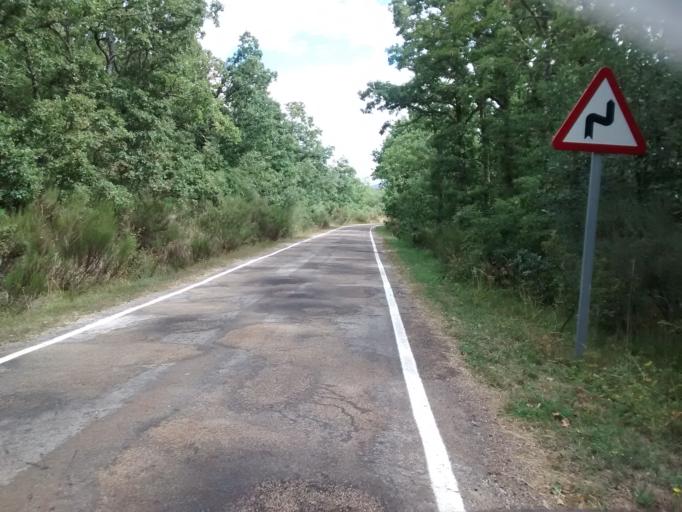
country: ES
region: Castille and Leon
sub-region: Provincia de Palencia
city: Polentinos
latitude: 42.9360
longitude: -4.4635
